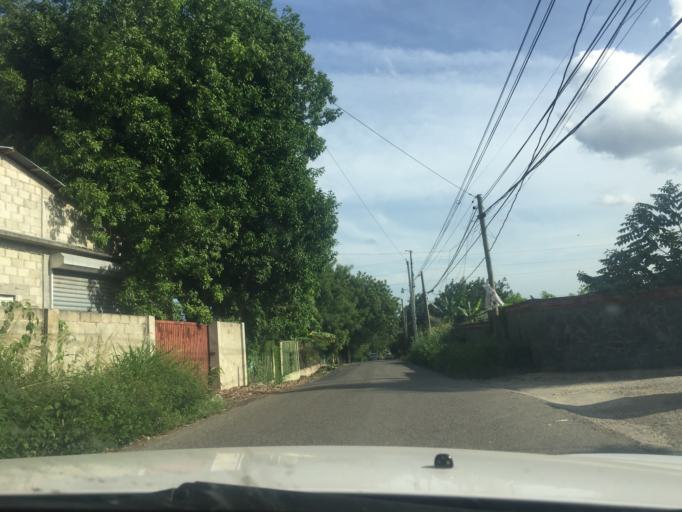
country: DO
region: Santiago
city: Tamboril
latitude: 19.4909
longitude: -70.6358
